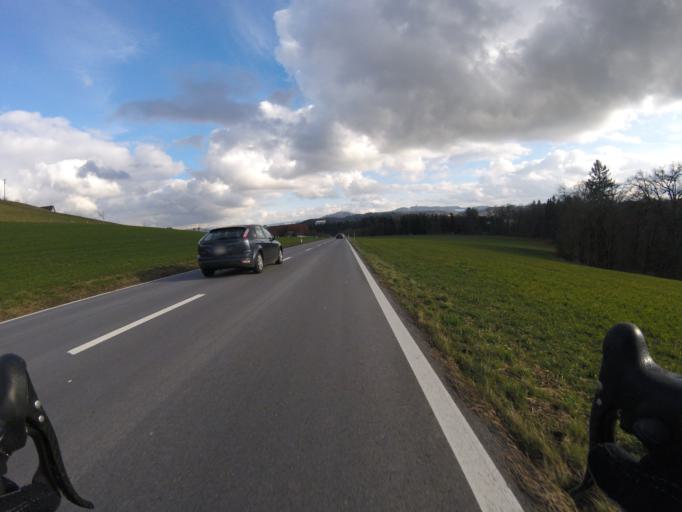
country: CH
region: Bern
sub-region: Bern-Mittelland District
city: Frauenkappelen
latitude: 46.9489
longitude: 7.3589
